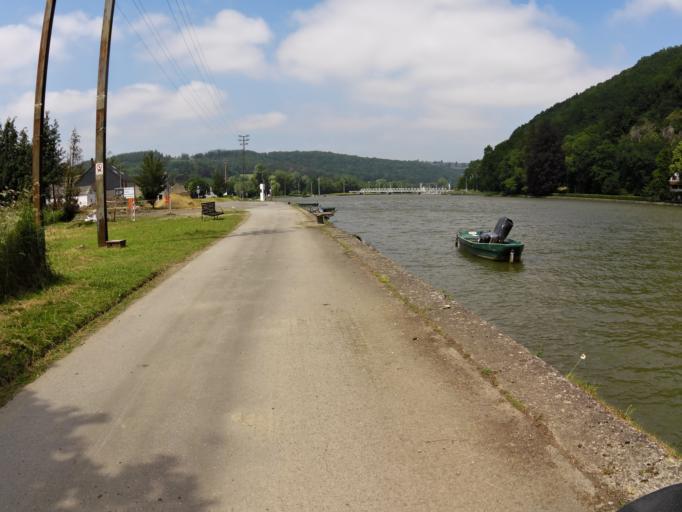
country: BE
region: Wallonia
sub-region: Province de Namur
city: Hastiere-Lavaux
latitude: 50.1961
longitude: 4.8216
